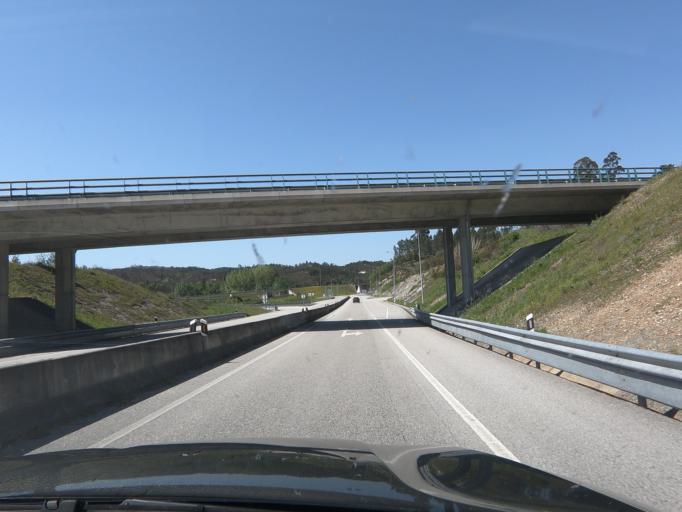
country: PT
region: Coimbra
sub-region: Vila Nova de Poiares
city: Poiares
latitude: 40.1729
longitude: -8.2673
